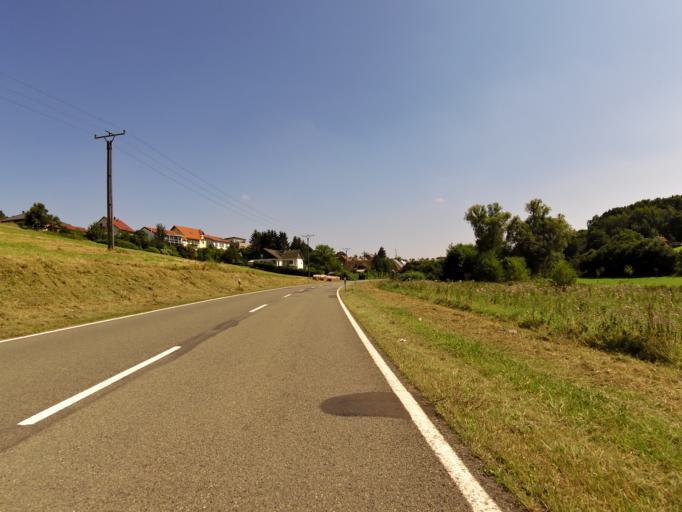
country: DE
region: Rheinland-Pfalz
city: Imsbach
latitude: 49.5850
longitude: 7.8719
